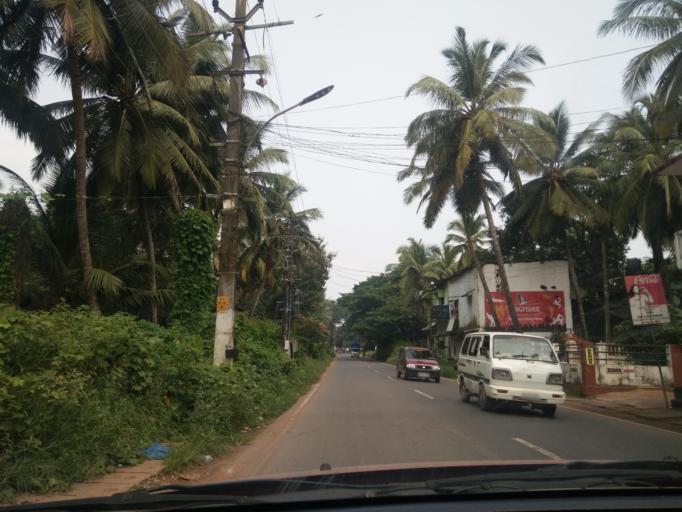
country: IN
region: Goa
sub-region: North Goa
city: Goa Velha
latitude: 15.4277
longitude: 73.8984
